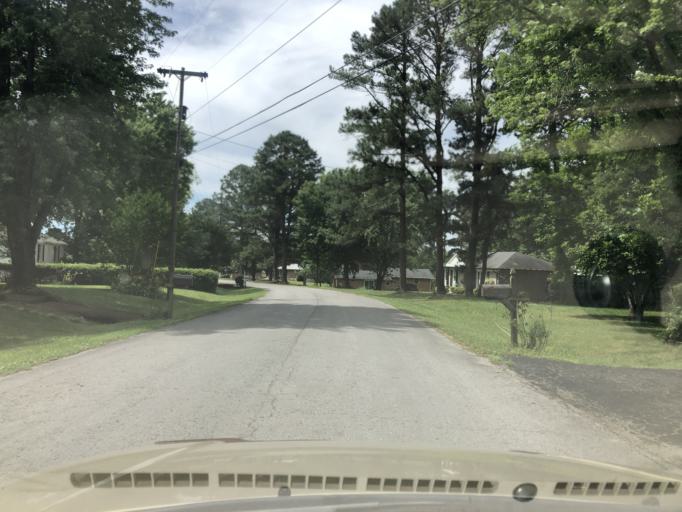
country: US
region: Tennessee
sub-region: Davidson County
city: Lakewood
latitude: 36.2606
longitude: -86.6242
